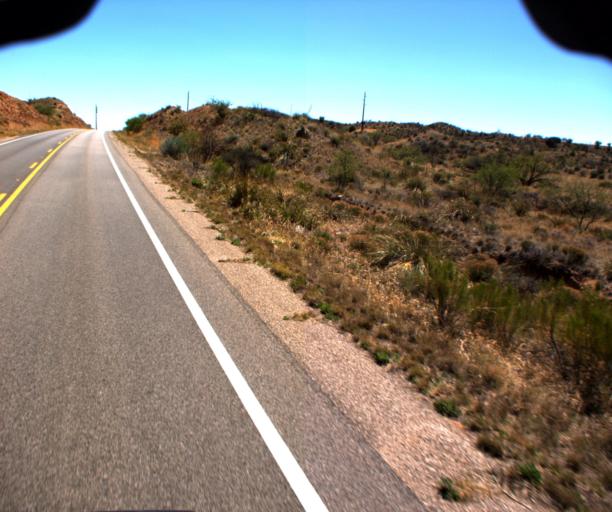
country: US
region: Arizona
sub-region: Pima County
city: Corona de Tucson
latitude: 31.7270
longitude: -110.6574
